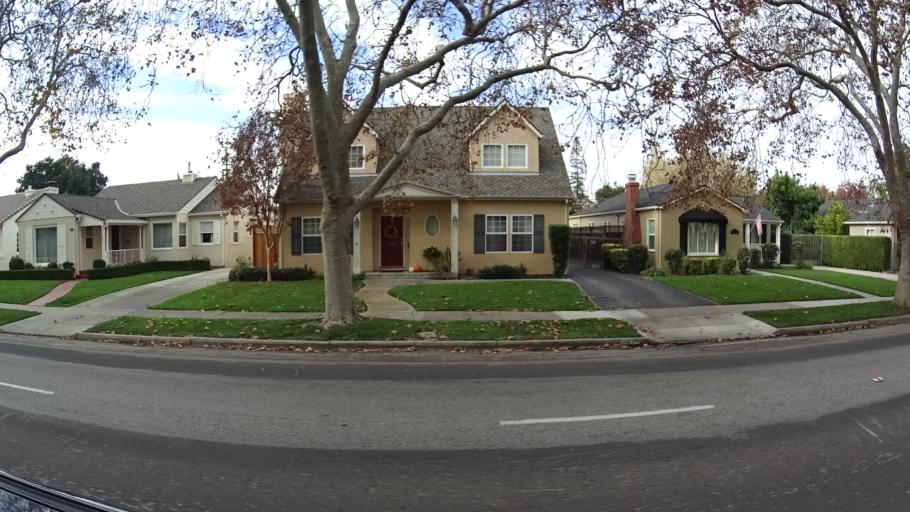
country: US
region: California
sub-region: Santa Clara County
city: Burbank
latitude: 37.3292
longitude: -121.9302
